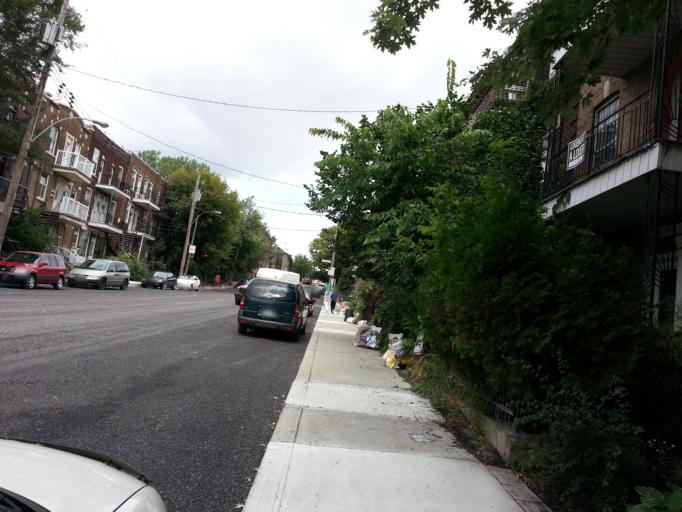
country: CA
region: Quebec
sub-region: Montreal
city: Montreal
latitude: 45.5328
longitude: -73.5602
